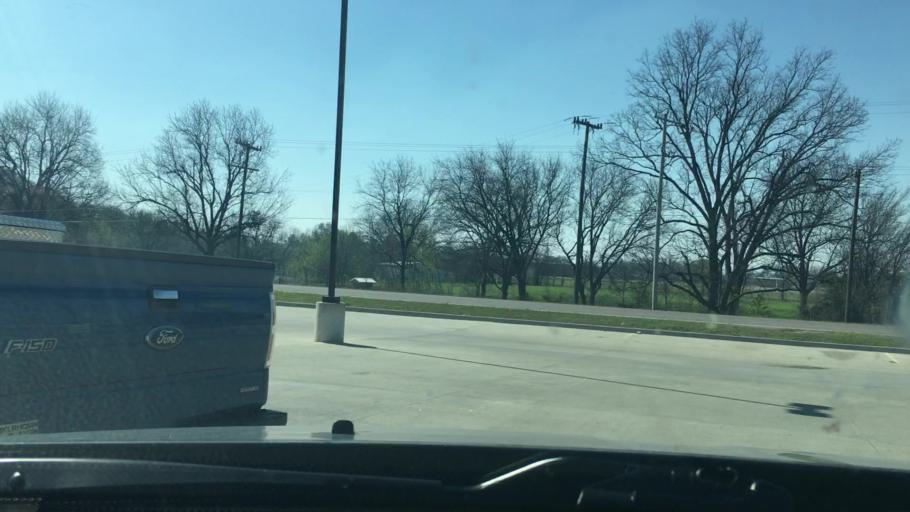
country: US
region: Oklahoma
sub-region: Johnston County
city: Tishomingo
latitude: 34.2309
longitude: -96.6600
